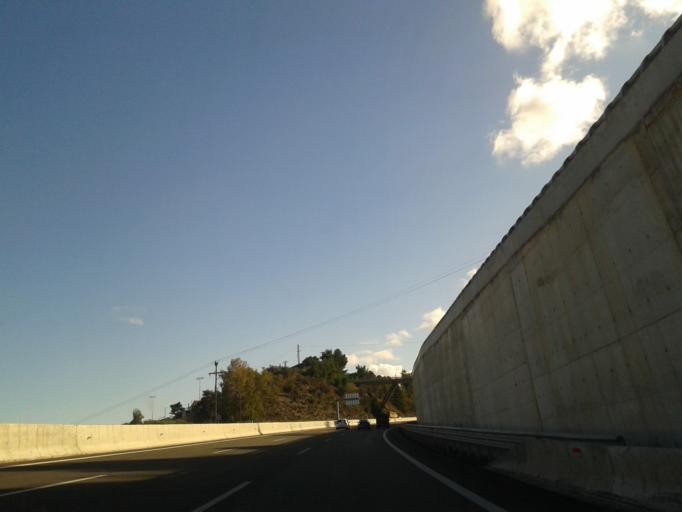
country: GR
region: West Greece
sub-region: Nomos Achaias
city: Aigio
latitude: 38.2552
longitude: 22.0668
